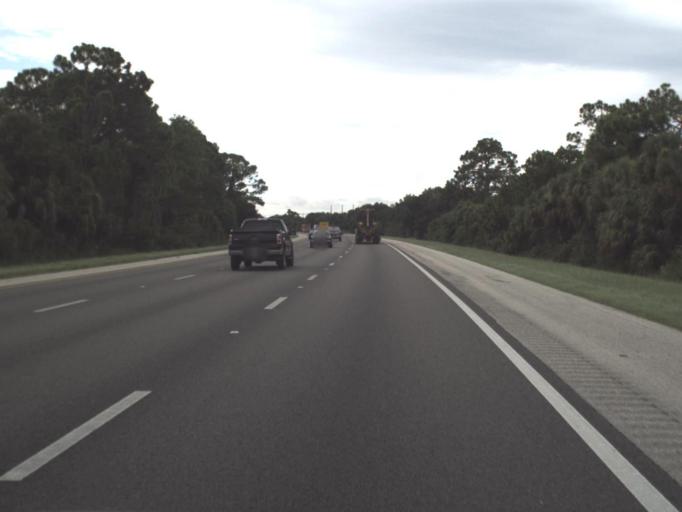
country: US
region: Florida
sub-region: Sarasota County
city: Vamo
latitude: 27.2287
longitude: -82.4524
